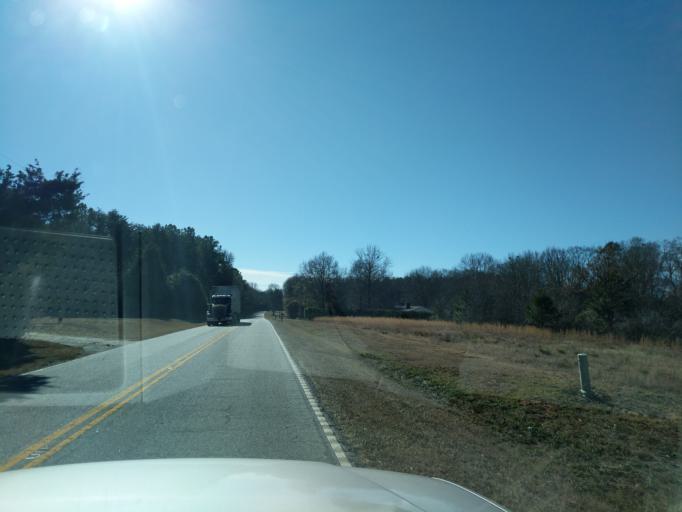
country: US
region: South Carolina
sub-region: Laurens County
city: Joanna
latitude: 34.3770
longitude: -81.8599
